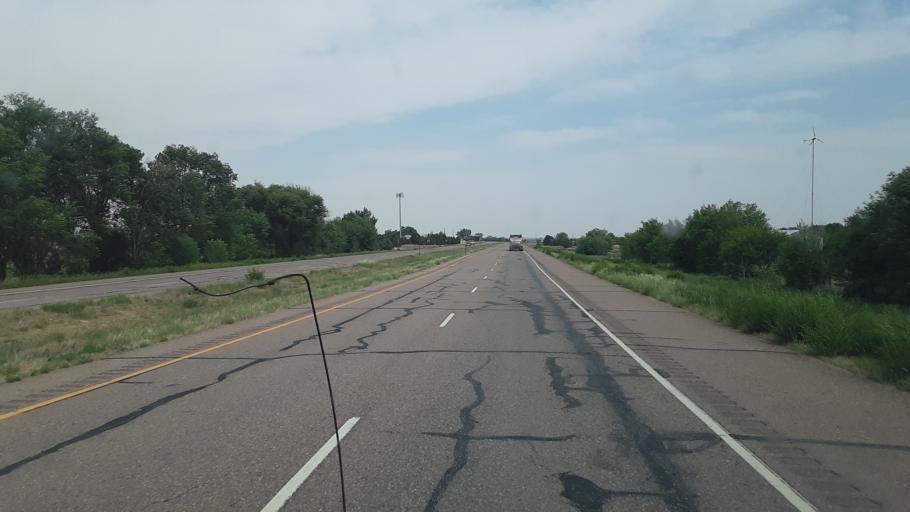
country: US
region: Colorado
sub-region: Fremont County
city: Penrose
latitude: 38.4059
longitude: -104.9938
